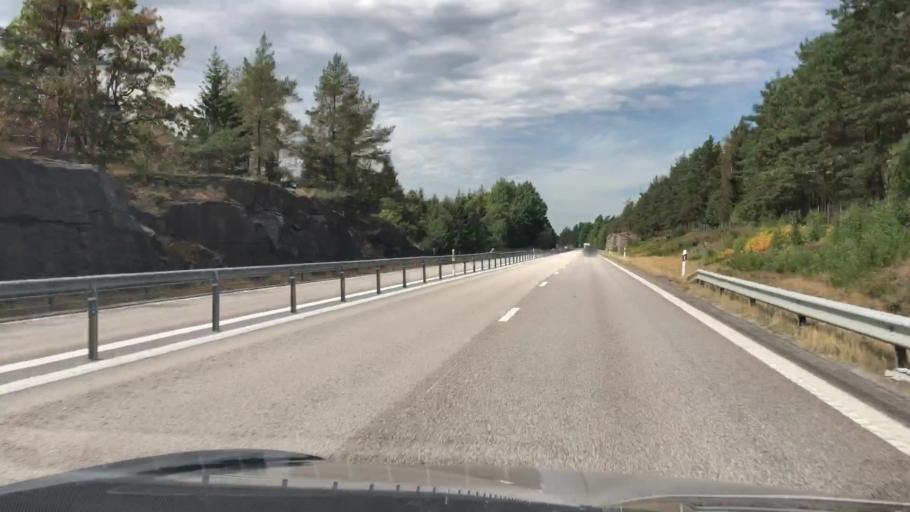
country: SE
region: Blekinge
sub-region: Ronneby Kommun
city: Brakne-Hoby
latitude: 56.2196
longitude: 15.1612
